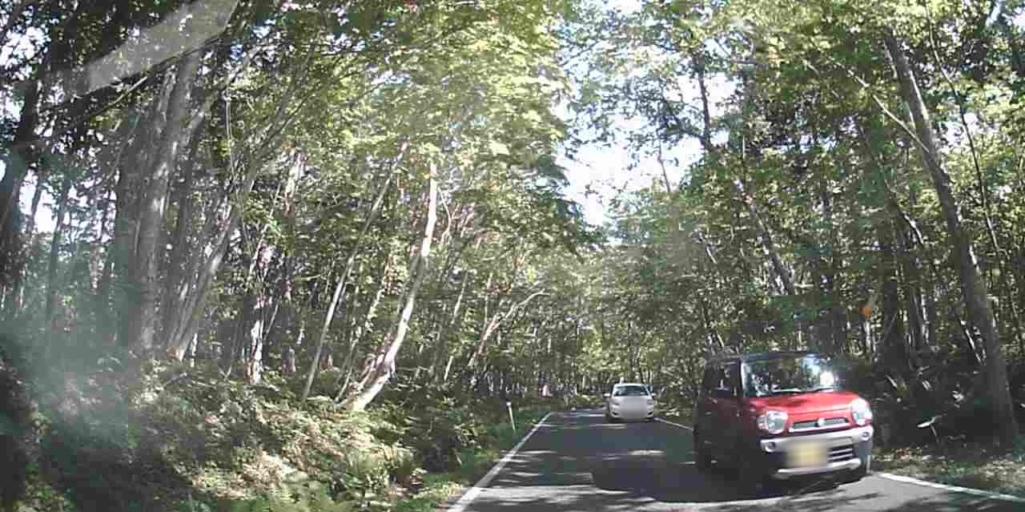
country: JP
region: Hokkaido
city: Shiraoi
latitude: 42.7221
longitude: 141.4116
